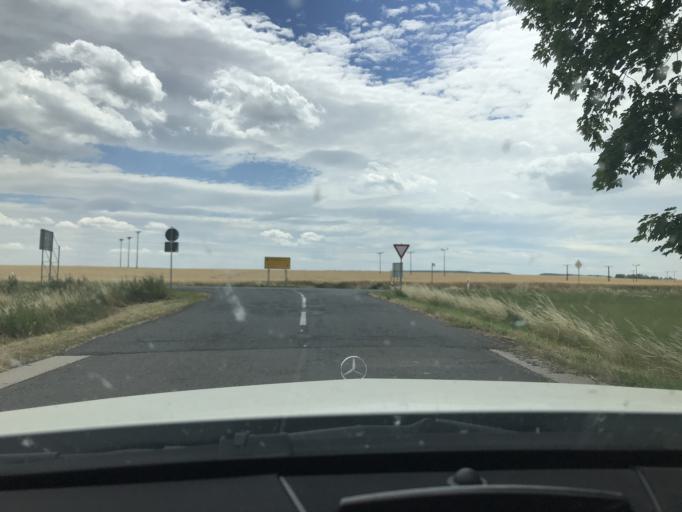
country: DE
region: Thuringia
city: Ebeleben
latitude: 51.2788
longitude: 10.7224
